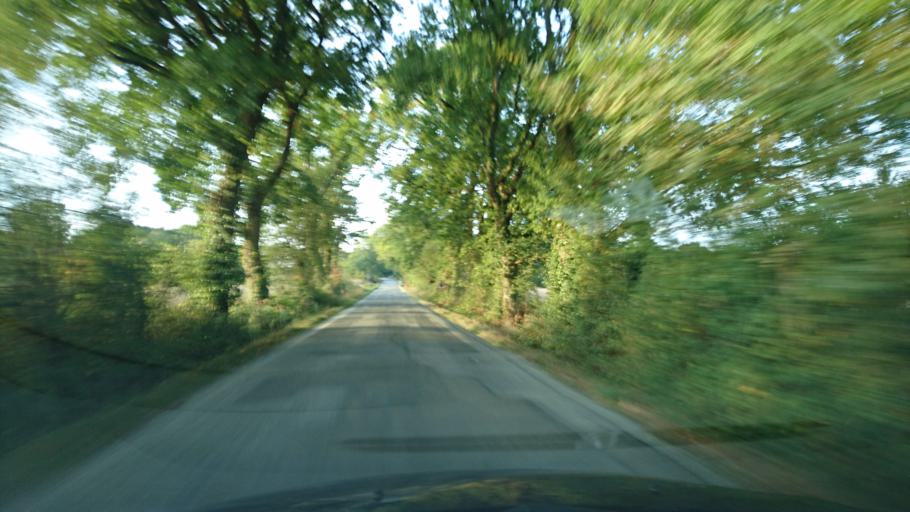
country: FR
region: Brittany
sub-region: Departement d'Ille-et-Vilaine
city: Bains-sur-Oust
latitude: 47.7412
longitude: -2.0513
